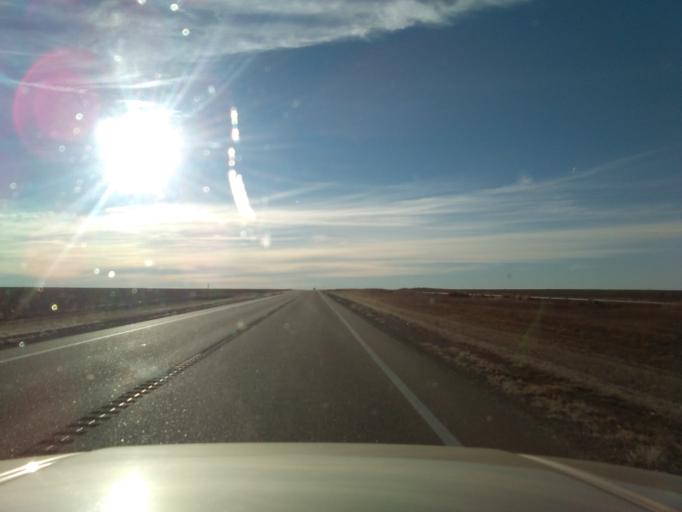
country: US
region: Kansas
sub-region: Sheridan County
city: Hoxie
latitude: 39.5297
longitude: -100.6012
